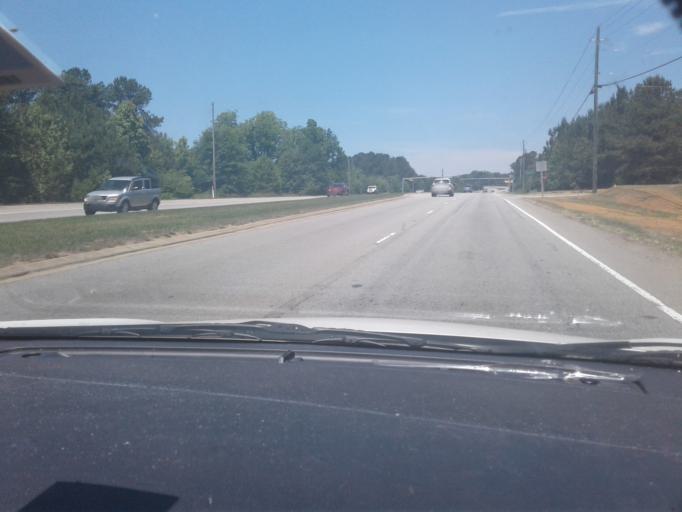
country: US
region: North Carolina
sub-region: Wake County
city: Holly Springs
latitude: 35.6309
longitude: -78.8255
